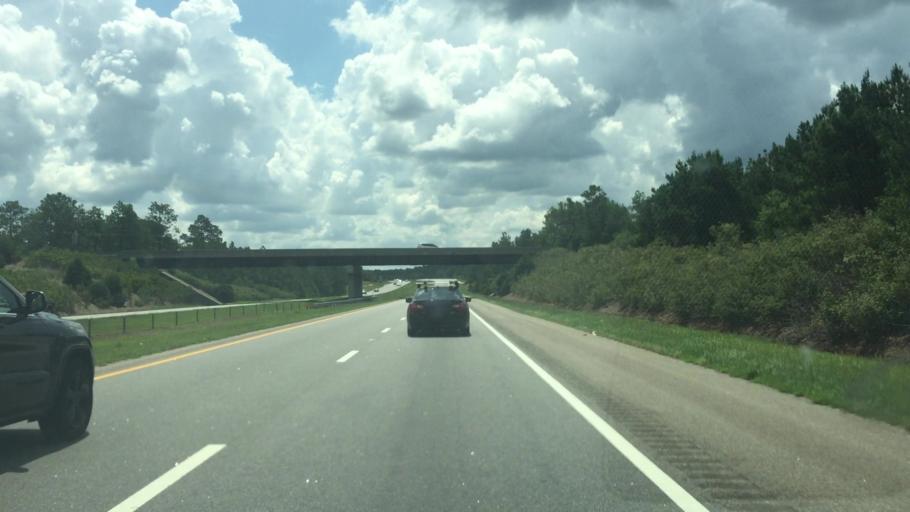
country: US
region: North Carolina
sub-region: Richmond County
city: Hamlet
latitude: 34.8592
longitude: -79.7441
